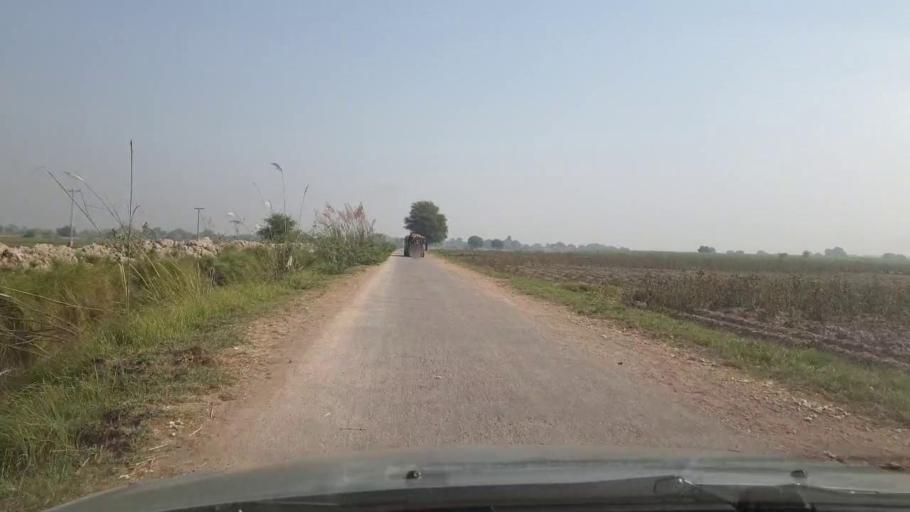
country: PK
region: Sindh
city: Tando Jam
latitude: 25.2912
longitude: 68.5239
